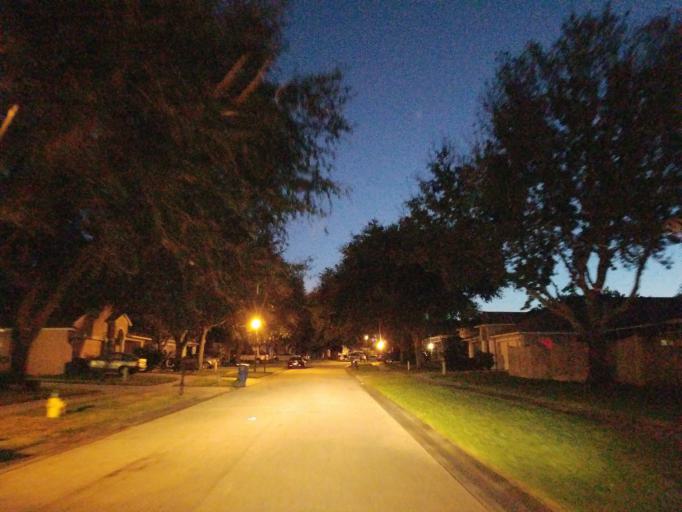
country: US
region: Florida
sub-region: Hillsborough County
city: Bloomingdale
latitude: 27.8988
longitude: -82.2120
